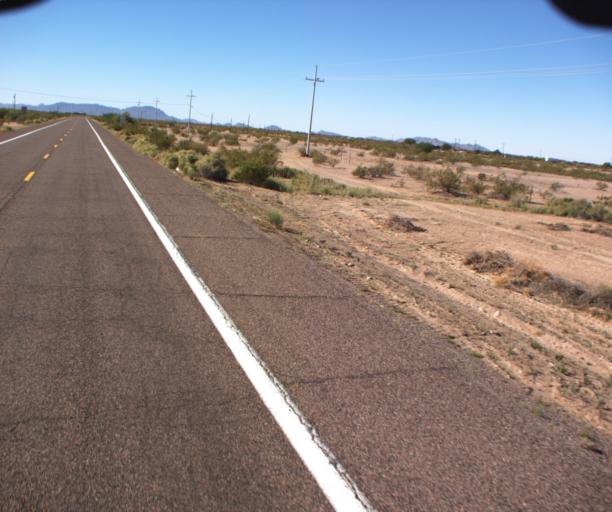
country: US
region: Arizona
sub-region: Maricopa County
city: Gila Bend
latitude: 32.9267
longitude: -112.7342
